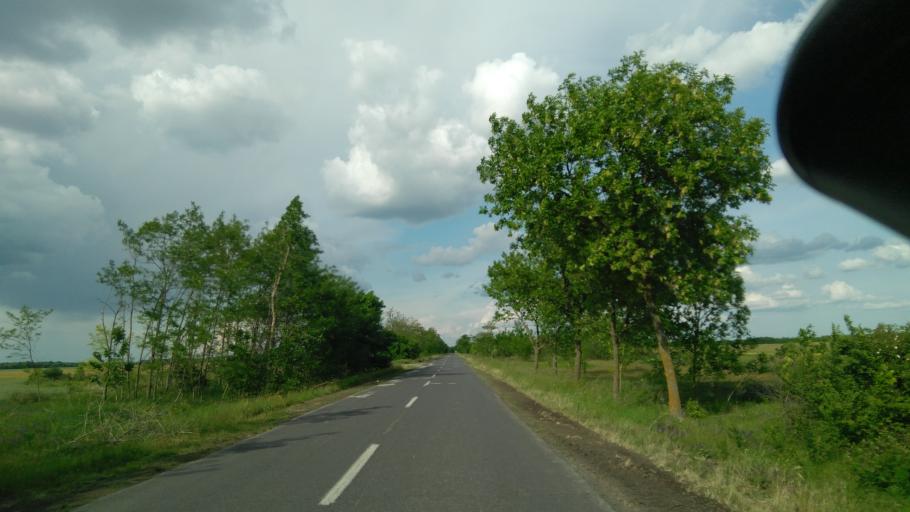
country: HU
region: Bekes
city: Battonya
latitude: 46.3110
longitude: 21.0696
